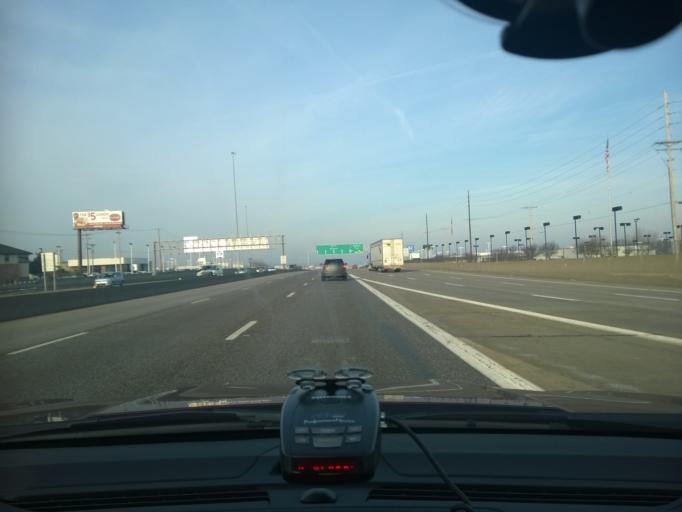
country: US
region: Missouri
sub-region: Saint Charles County
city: Saint Peters
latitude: 38.7985
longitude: -90.5961
